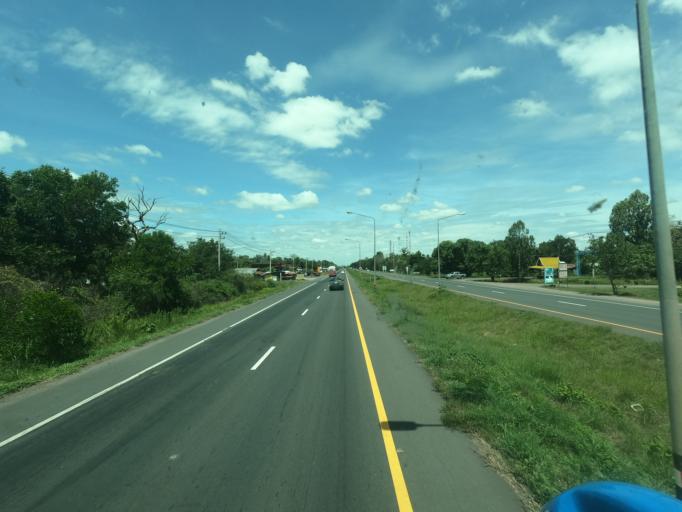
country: TH
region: Surin
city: Prasat
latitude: 14.6142
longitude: 103.3462
